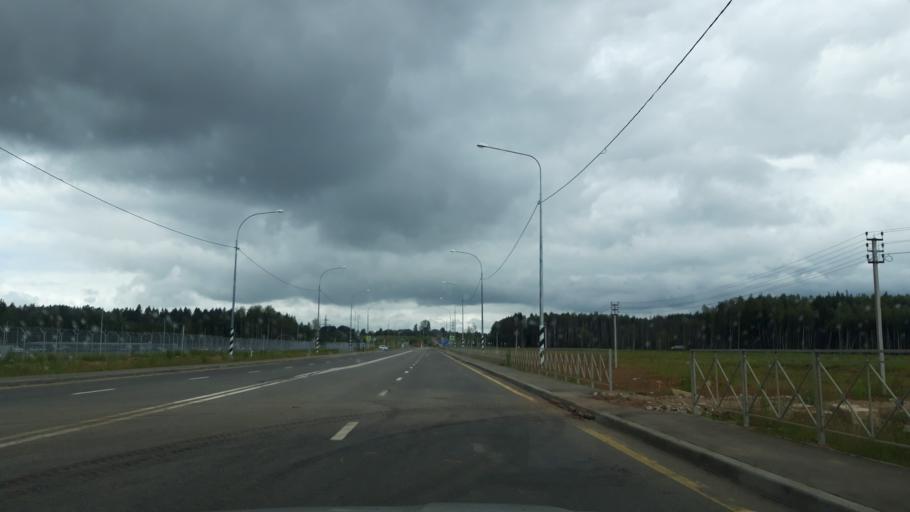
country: RU
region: Moskovskaya
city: Lozhki
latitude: 56.0848
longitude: 37.0845
